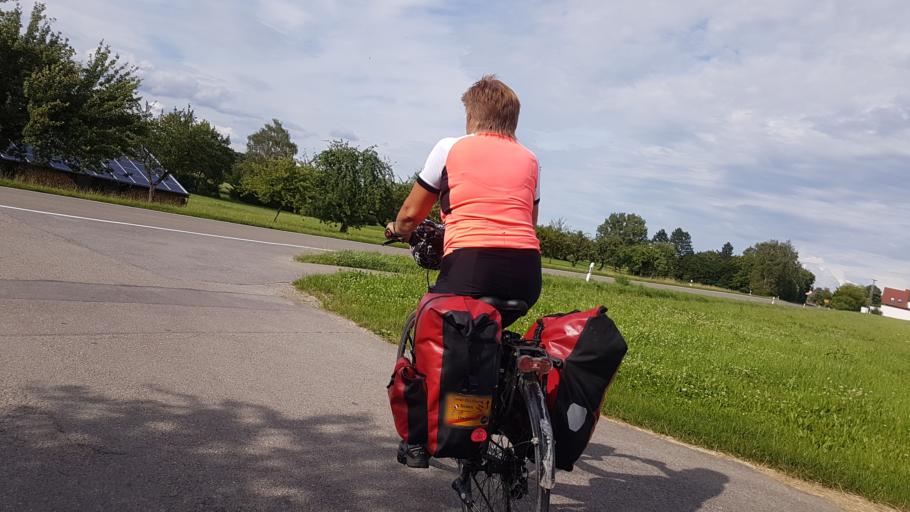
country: DE
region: Baden-Wuerttemberg
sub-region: Tuebingen Region
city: Rottenacker
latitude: 48.2301
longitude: 9.6768
